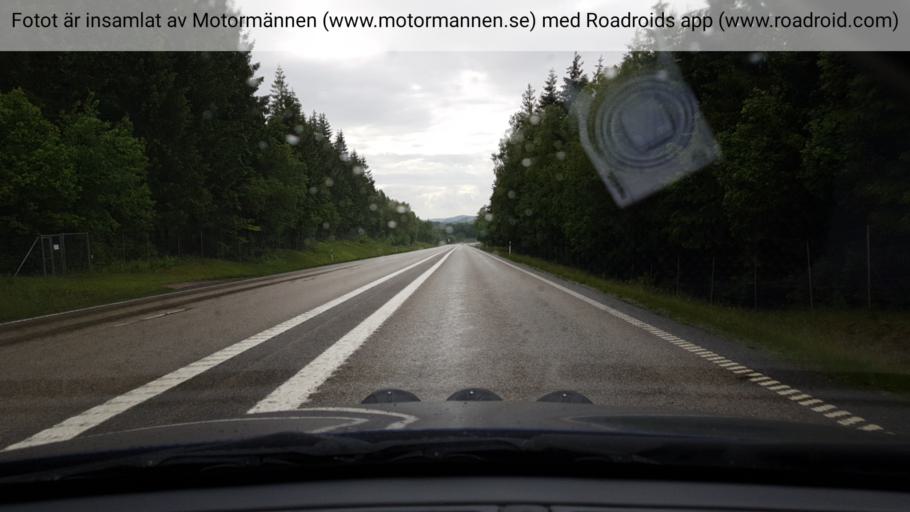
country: SE
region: Vaestra Goetaland
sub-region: Marks Kommun
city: Fritsla
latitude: 57.5148
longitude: 12.7558
